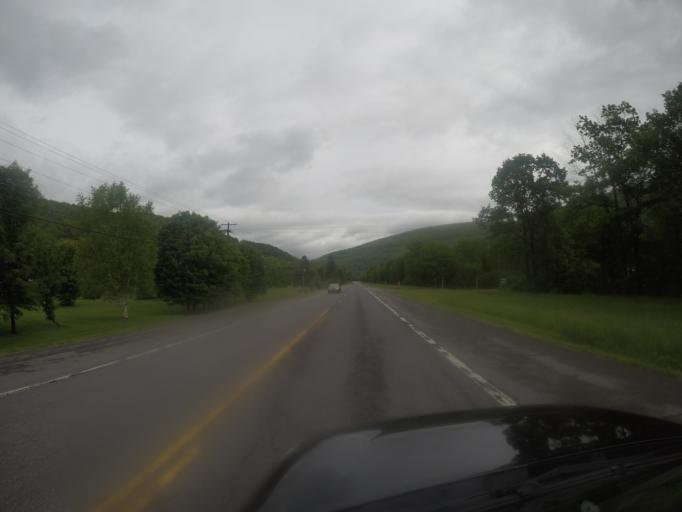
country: US
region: New York
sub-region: Ulster County
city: Shokan
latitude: 42.0670
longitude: -74.3075
